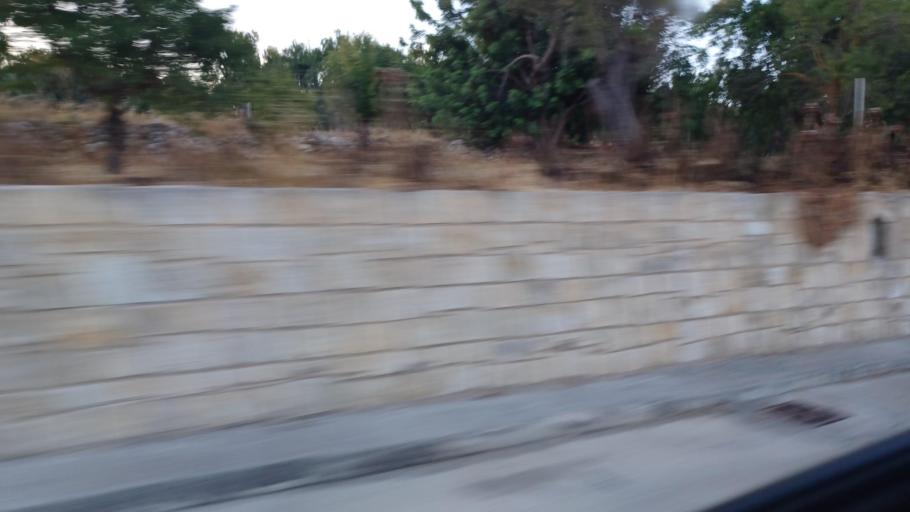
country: CY
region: Pafos
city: Mesogi
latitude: 34.8197
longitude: 32.5819
